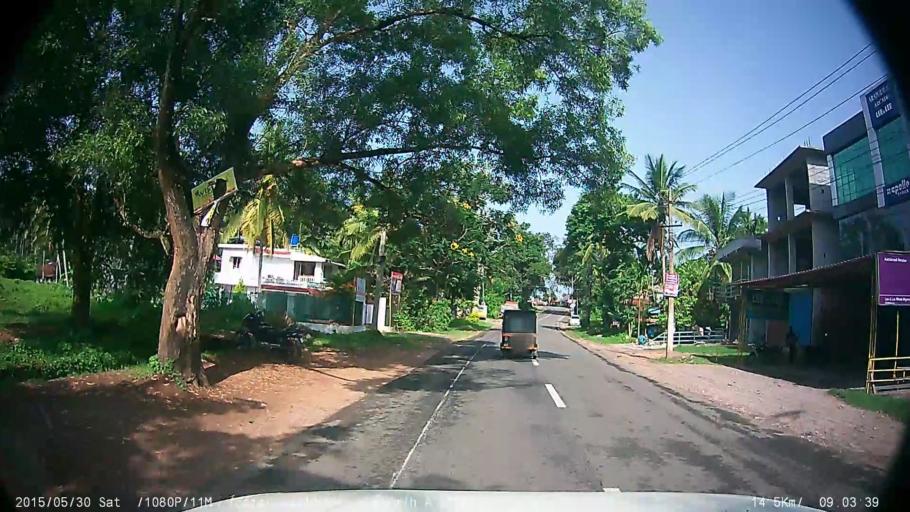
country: IN
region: Kerala
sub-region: Wayanad
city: Panamaram
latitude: 11.6685
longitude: 76.2691
